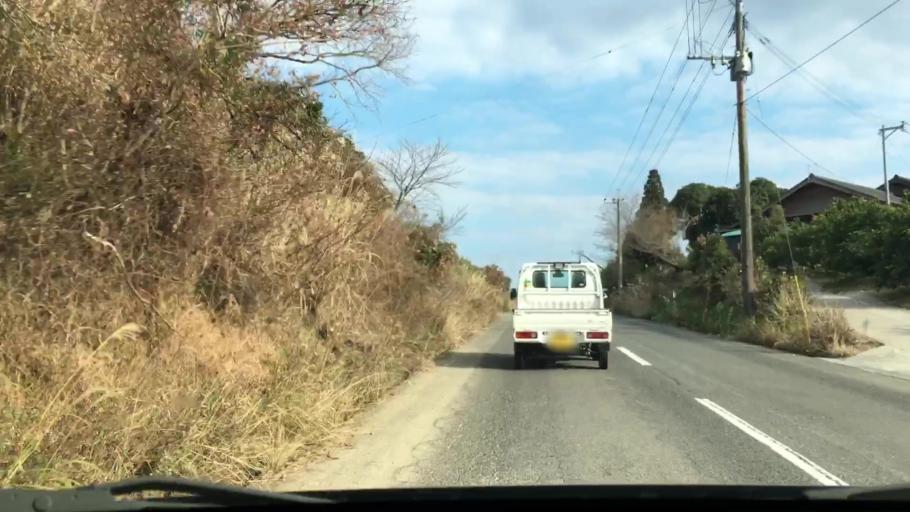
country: JP
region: Miyazaki
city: Nichinan
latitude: 31.5991
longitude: 131.3208
